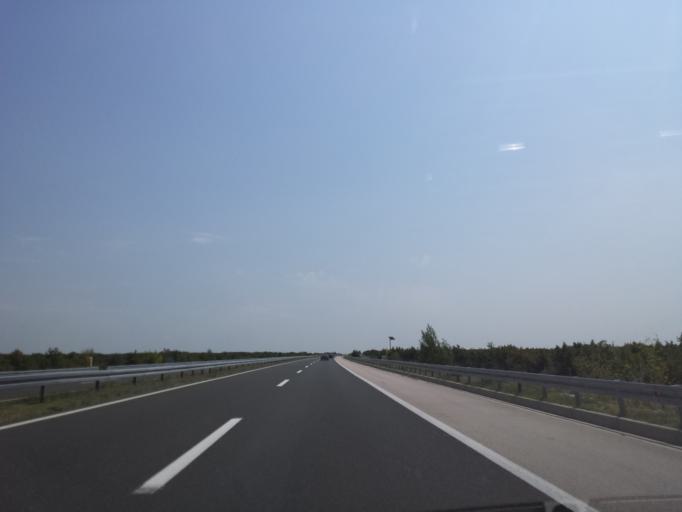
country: HR
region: Zadarska
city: Benkovac
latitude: 43.9870
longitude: 15.6284
